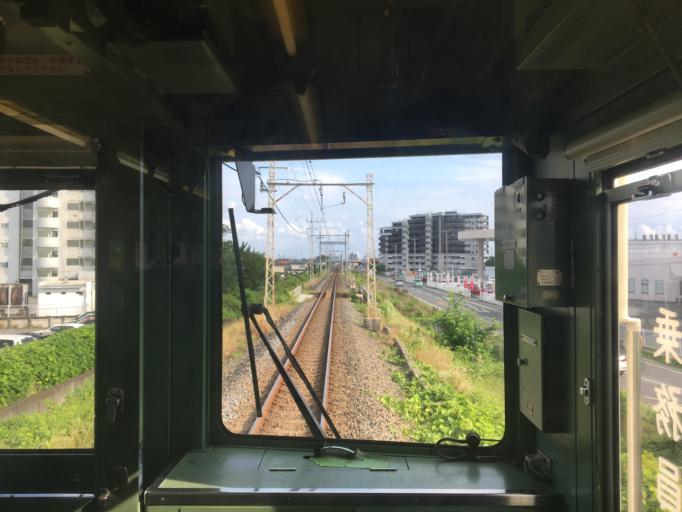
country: JP
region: Tochigi
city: Ashikaga
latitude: 36.3221
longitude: 139.4534
